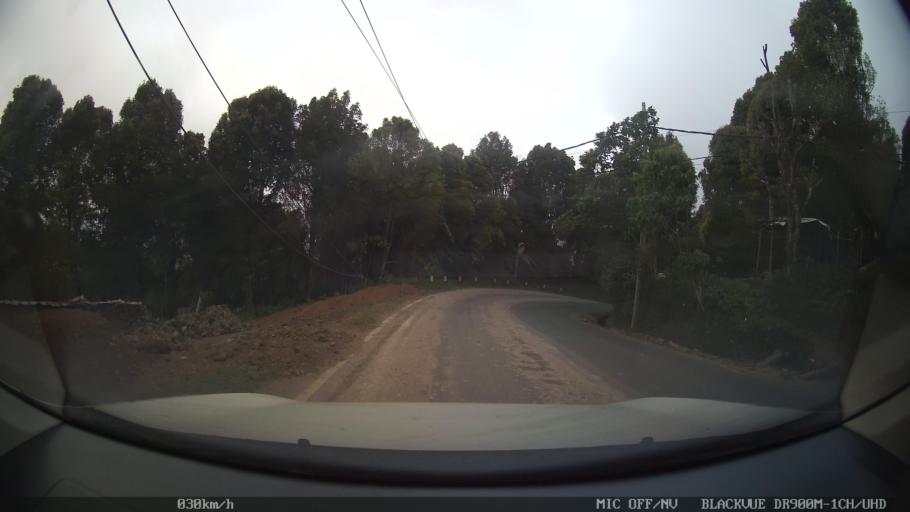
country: ID
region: Bali
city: Banjar Ambengan
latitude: -8.2125
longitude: 115.1431
